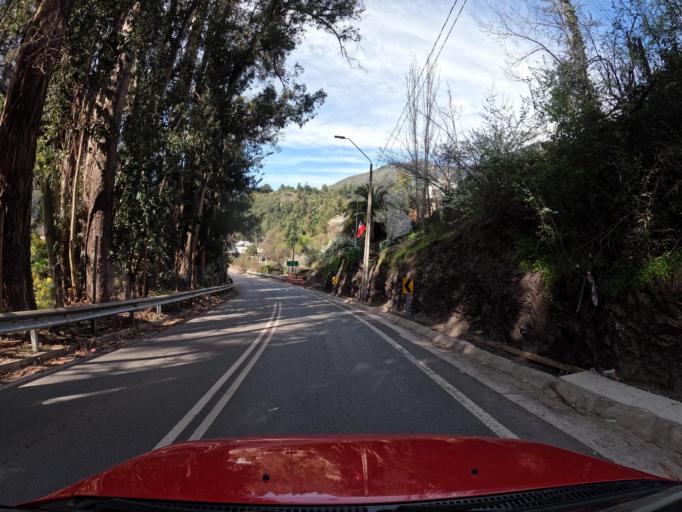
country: CL
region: O'Higgins
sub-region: Provincia de Colchagua
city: Chimbarongo
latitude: -35.0013
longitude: -70.8134
